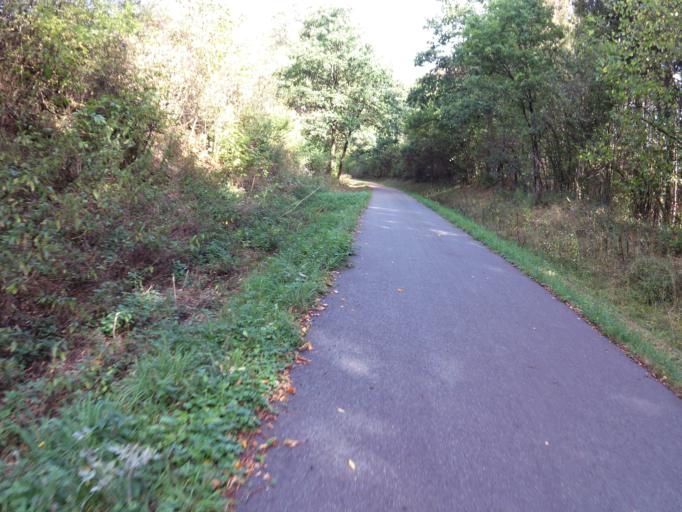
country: DE
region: Rheinland-Pfalz
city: Kickeshausen
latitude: 50.0634
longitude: 6.2469
